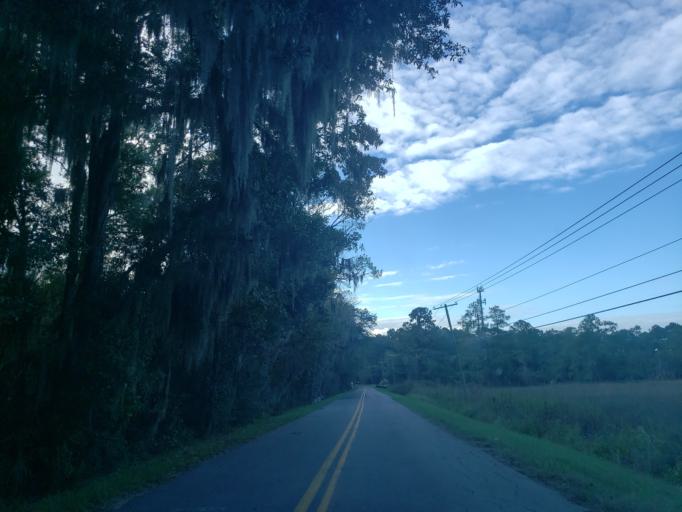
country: US
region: Georgia
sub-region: Chatham County
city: Georgetown
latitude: 31.9927
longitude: -81.2364
